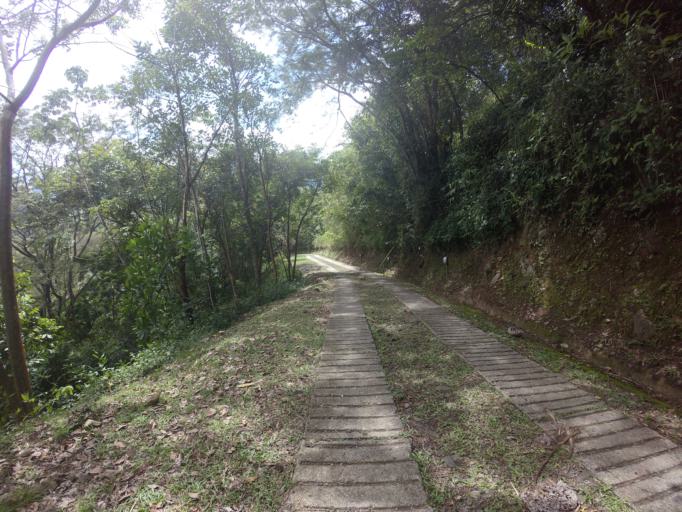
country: CO
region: Antioquia
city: Tarso
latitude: 5.8696
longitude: -75.7610
